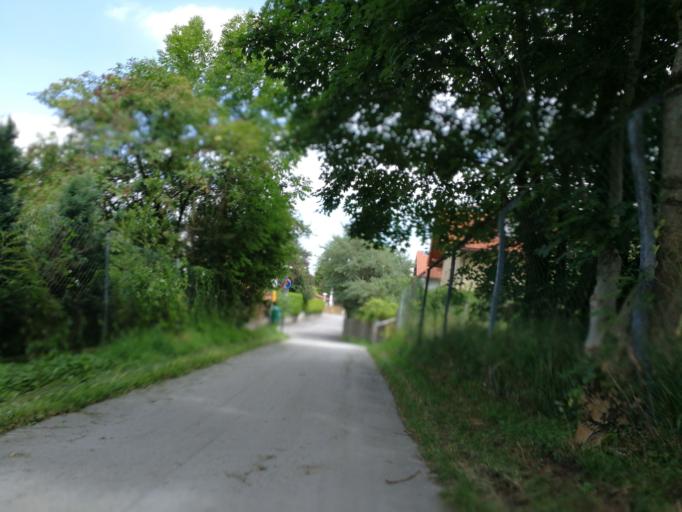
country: DE
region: Bavaria
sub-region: Upper Bavaria
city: Ainring
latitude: 47.8056
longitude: 12.9825
